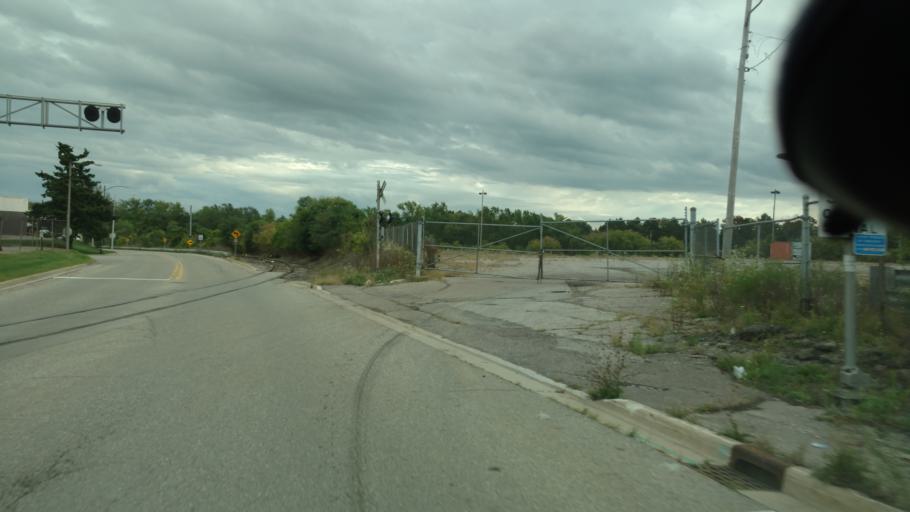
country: US
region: Michigan
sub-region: Ingham County
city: Edgemont Park
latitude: 42.7249
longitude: -84.5821
